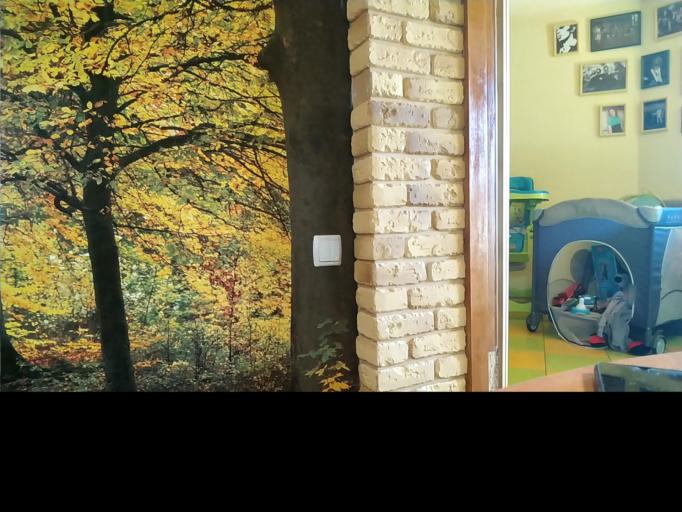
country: RU
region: Tverskaya
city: Kuzhenkino
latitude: 57.5294
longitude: 34.1268
